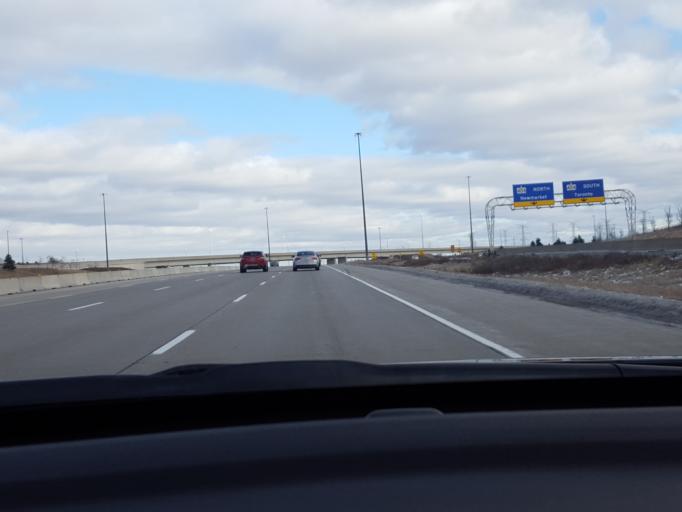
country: CA
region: Ontario
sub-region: York
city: Richmond Hill
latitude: 43.8375
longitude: -79.3761
